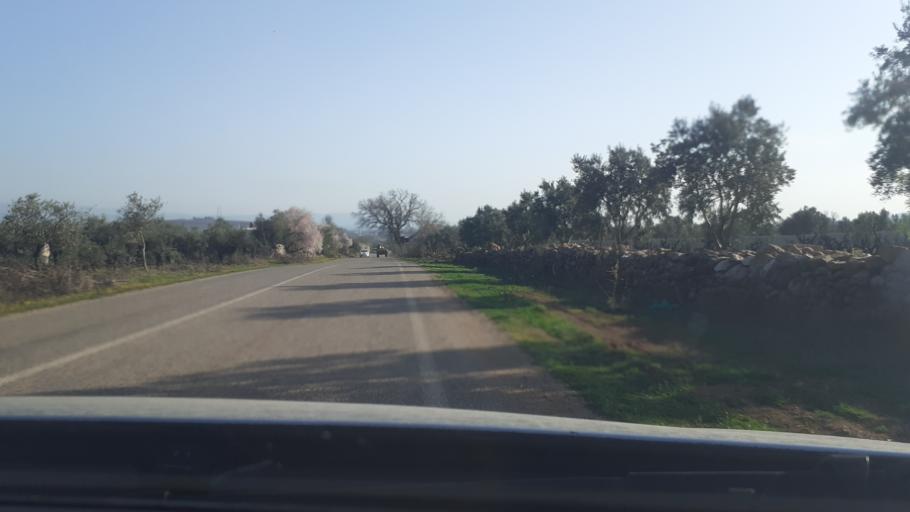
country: TR
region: Hatay
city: Aktepe
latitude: 36.7245
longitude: 36.4850
